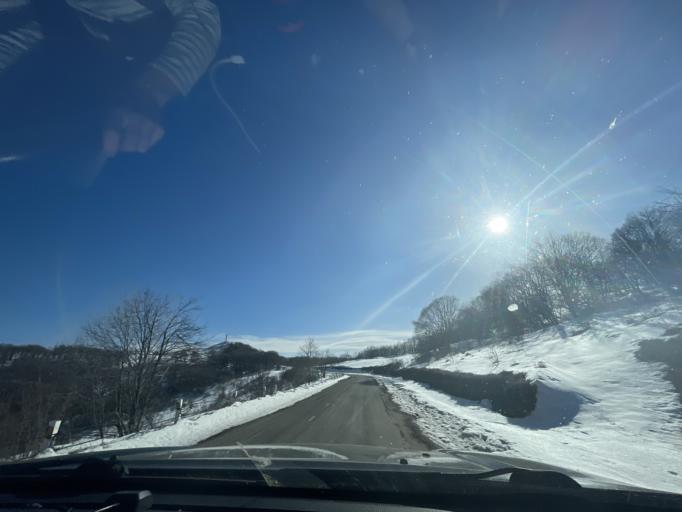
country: GE
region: Kvemo Kartli
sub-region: Tetri Tsqaro
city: Manglisi
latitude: 41.7664
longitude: 44.5067
